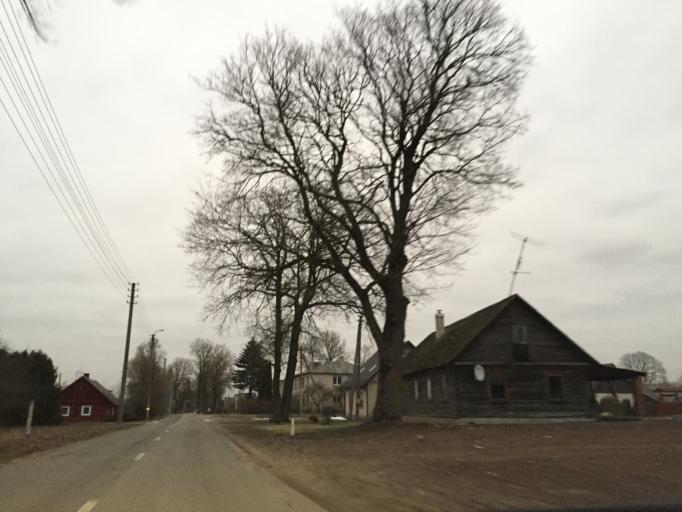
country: LT
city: Zagare
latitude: 56.3423
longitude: 23.3036
